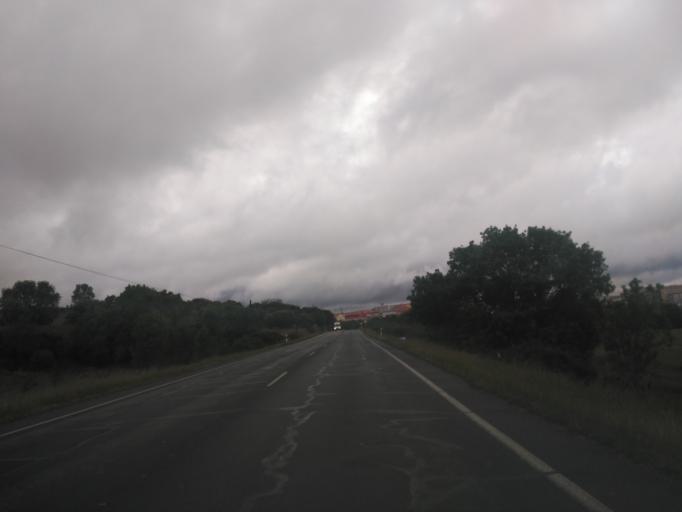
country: ES
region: Castille and Leon
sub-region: Provincia de Salamanca
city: Fuentes de Bejar
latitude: 40.5287
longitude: -5.6758
